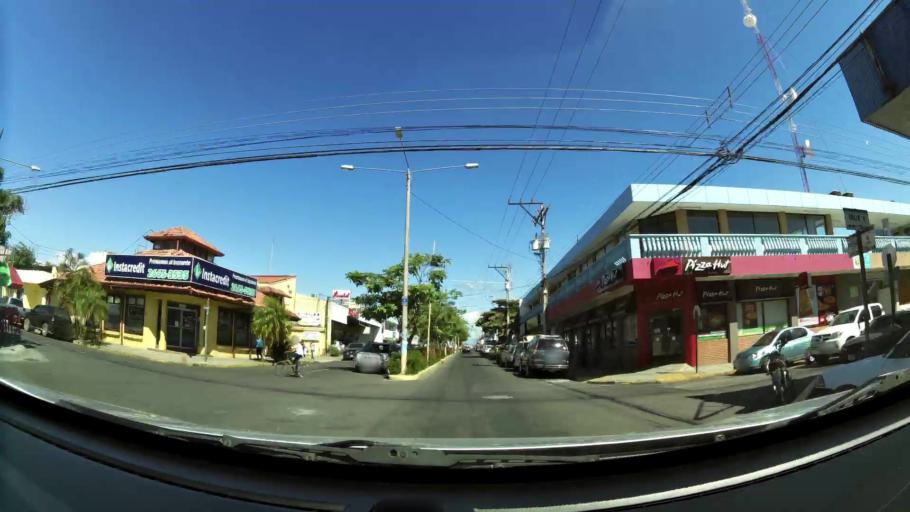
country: CR
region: Guanacaste
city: Liberia
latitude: 10.6284
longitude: -85.4401
